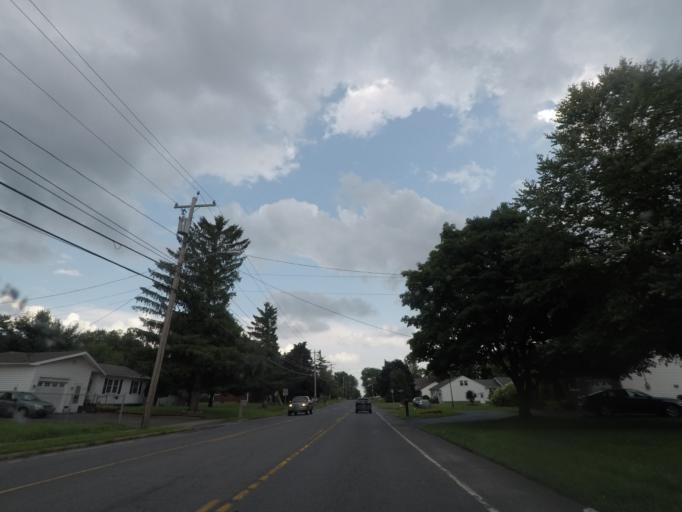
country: US
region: New York
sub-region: Albany County
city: Roessleville
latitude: 42.7014
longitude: -73.7961
